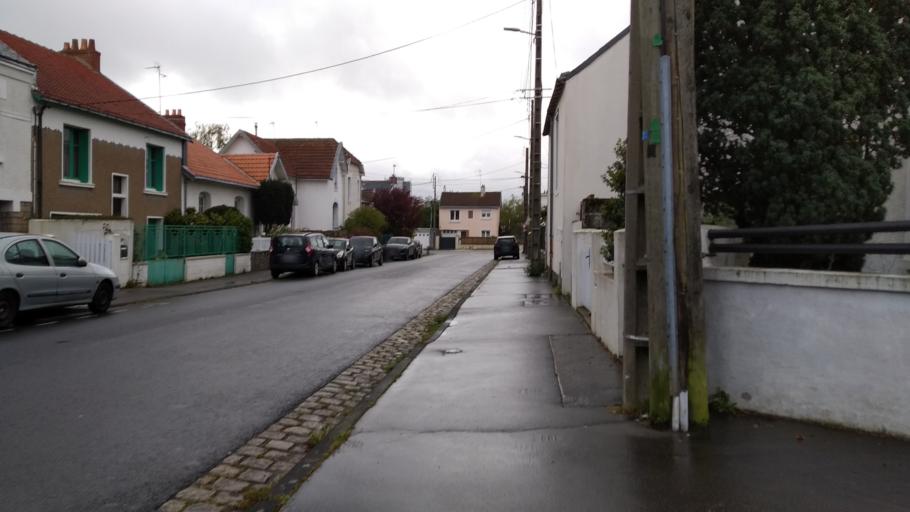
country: FR
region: Pays de la Loire
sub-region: Departement de la Loire-Atlantique
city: Nantes
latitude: 47.2145
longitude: -1.5915
